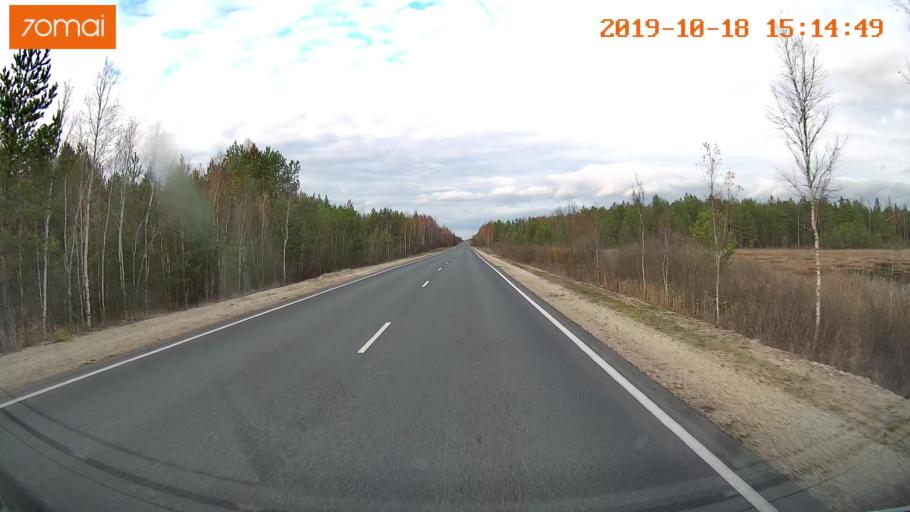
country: RU
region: Vladimir
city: Gus'-Khrustal'nyy
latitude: 55.6087
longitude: 40.7211
